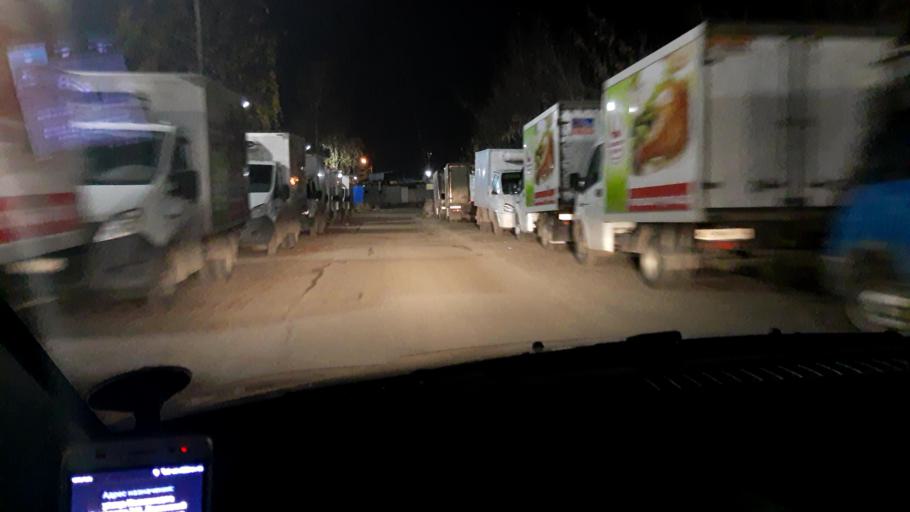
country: RU
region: Nizjnij Novgorod
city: Gorbatovka
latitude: 56.2519
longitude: 43.8757
